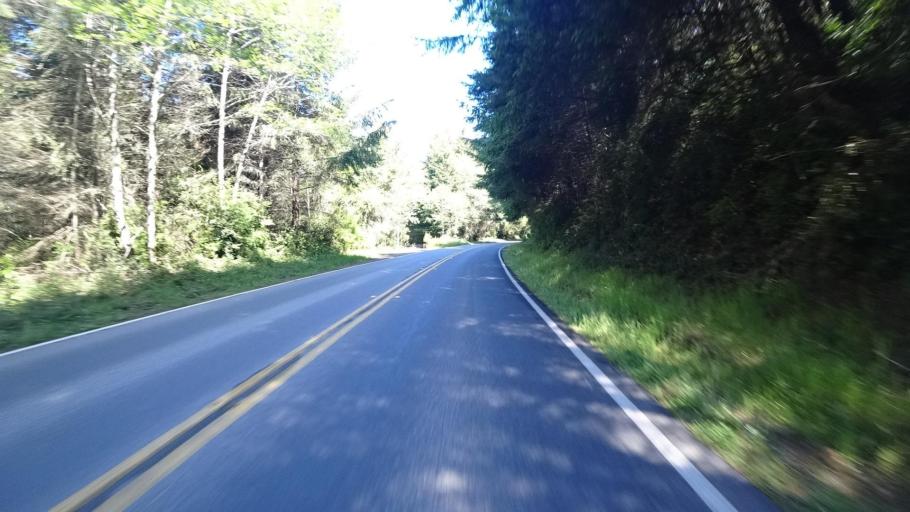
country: US
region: California
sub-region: Humboldt County
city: McKinleyville
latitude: 40.9607
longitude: -124.0719
